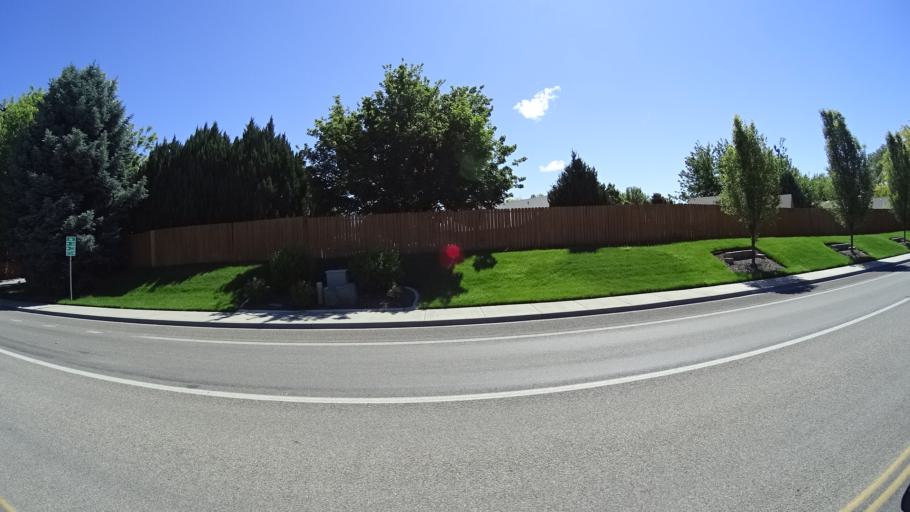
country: US
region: Idaho
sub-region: Ada County
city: Meridian
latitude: 43.6246
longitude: -116.3746
